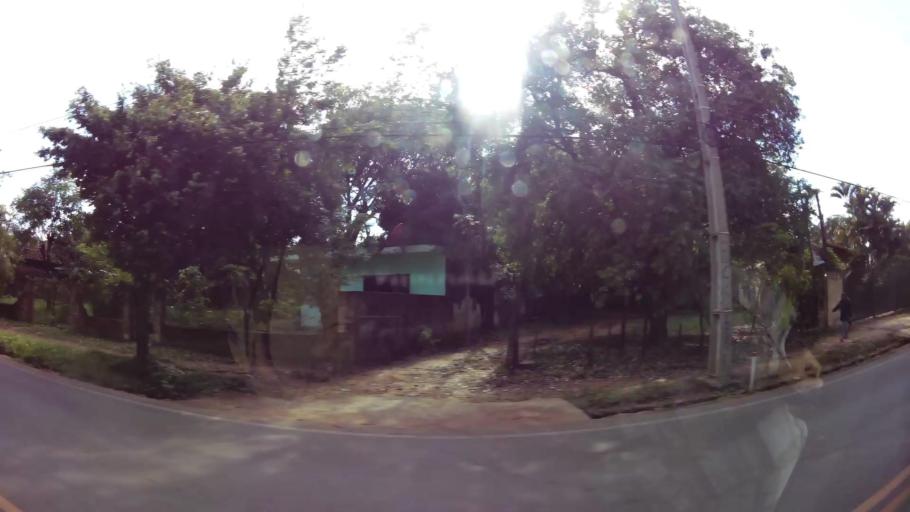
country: PY
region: Central
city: San Lorenzo
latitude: -25.2804
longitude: -57.4846
